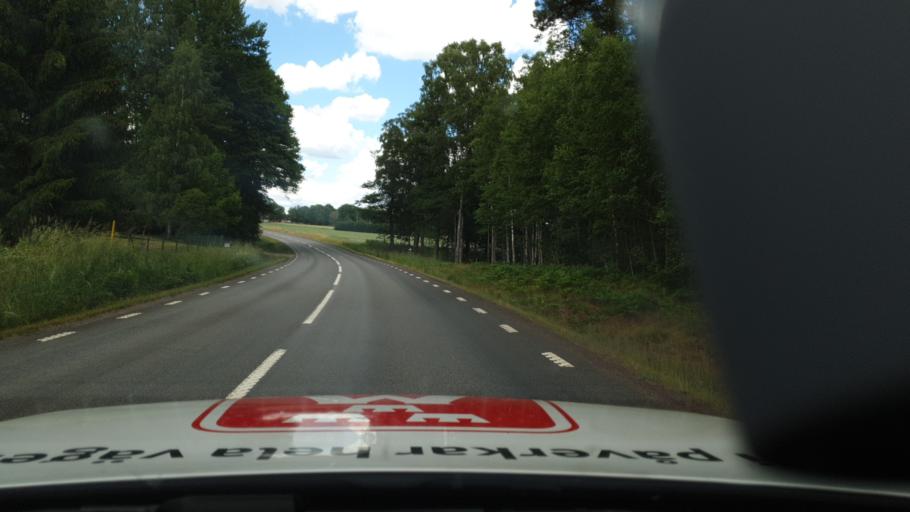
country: SE
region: Vaestra Goetaland
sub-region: Karlsborgs Kommun
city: Molltorp
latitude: 58.4311
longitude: 14.4007
